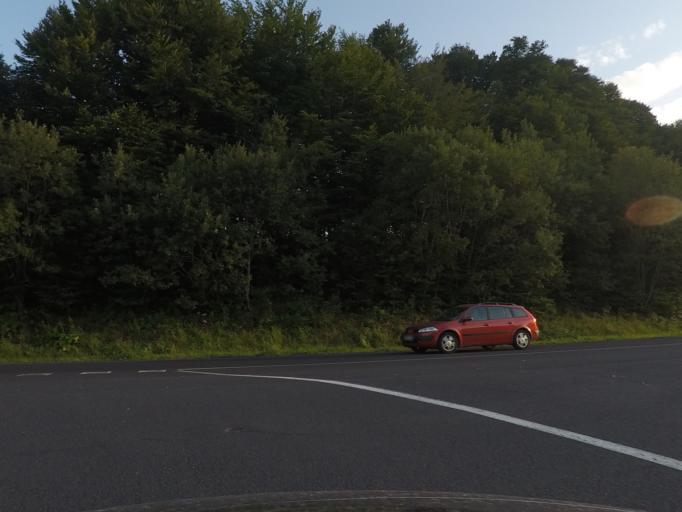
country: FR
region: Auvergne
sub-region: Departement du Puy-de-Dome
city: Mont-Dore
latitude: 45.5045
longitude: 2.8972
